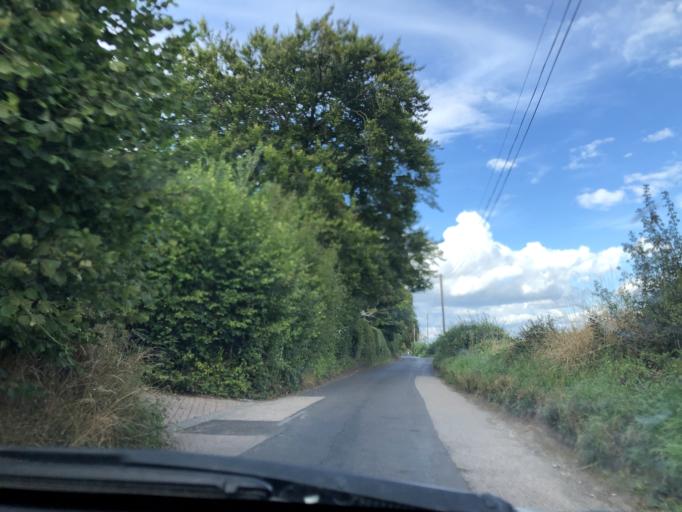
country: GB
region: England
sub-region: Kent
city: Eynsford
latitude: 51.3722
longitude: 0.2104
